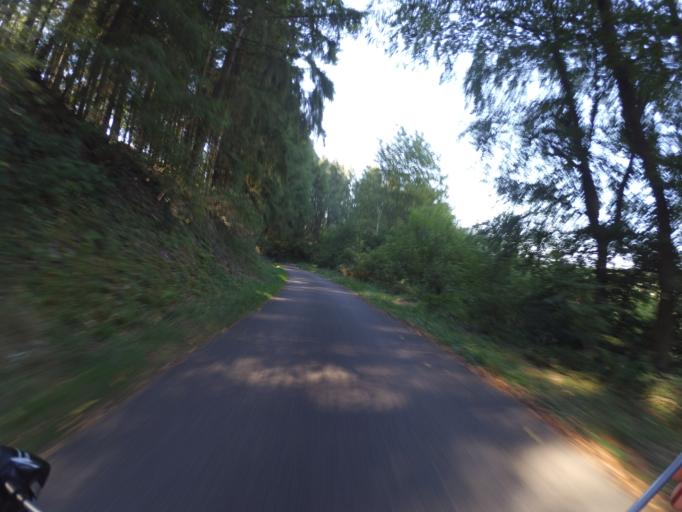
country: DE
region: Rheinland-Pfalz
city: Rivenich
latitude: 49.8690
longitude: 6.8463
